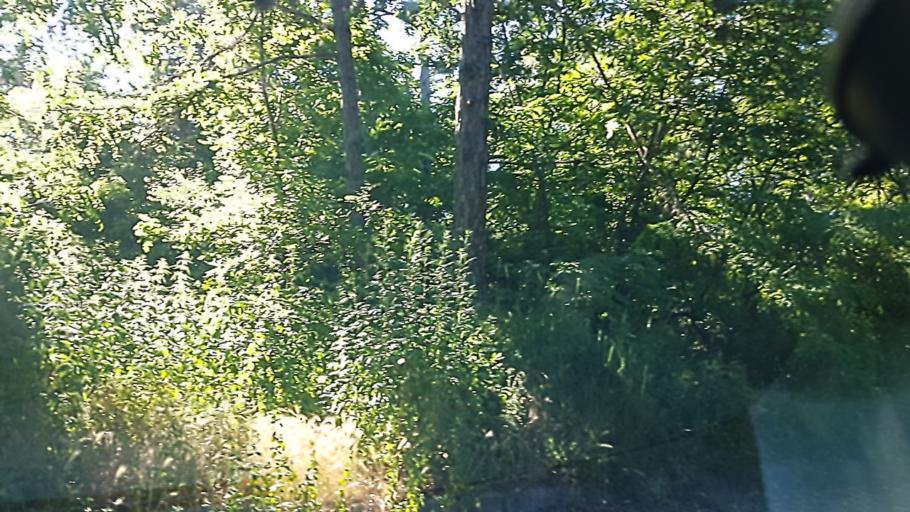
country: HU
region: Pest
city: Pilisszentivan
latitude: 47.6090
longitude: 18.8872
